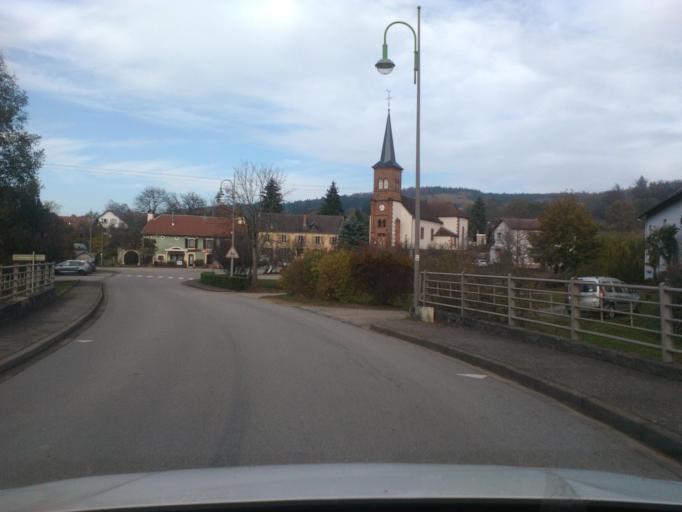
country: FR
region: Lorraine
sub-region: Departement des Vosges
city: Moyenmoutier
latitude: 48.3489
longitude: 6.9355
